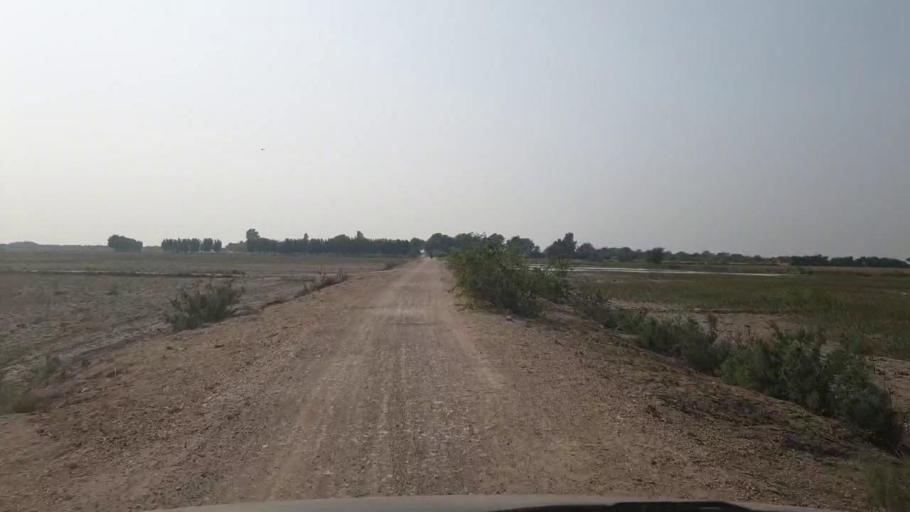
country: PK
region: Sindh
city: Tando Muhammad Khan
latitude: 25.0466
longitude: 68.3715
